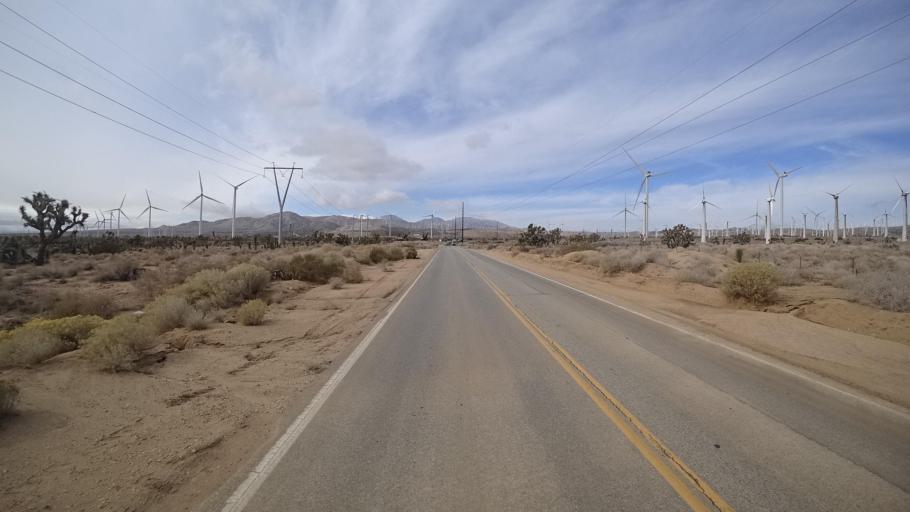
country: US
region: California
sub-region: Kern County
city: Mojave
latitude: 35.0383
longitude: -118.2936
